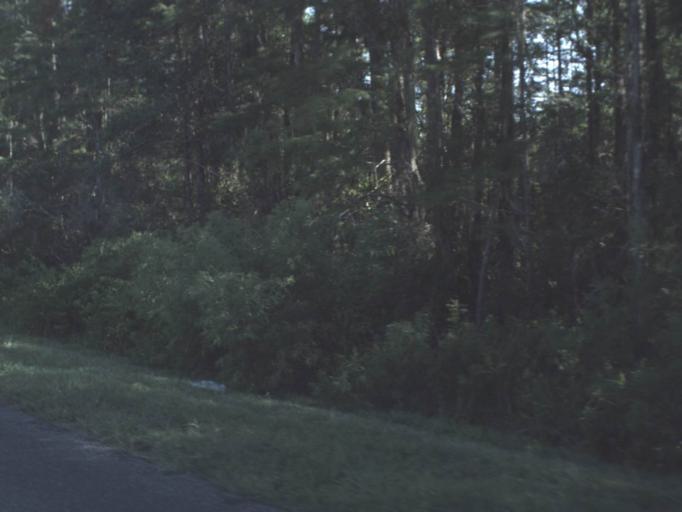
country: US
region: Florida
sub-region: Taylor County
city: Perry
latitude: 30.2257
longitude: -83.6159
